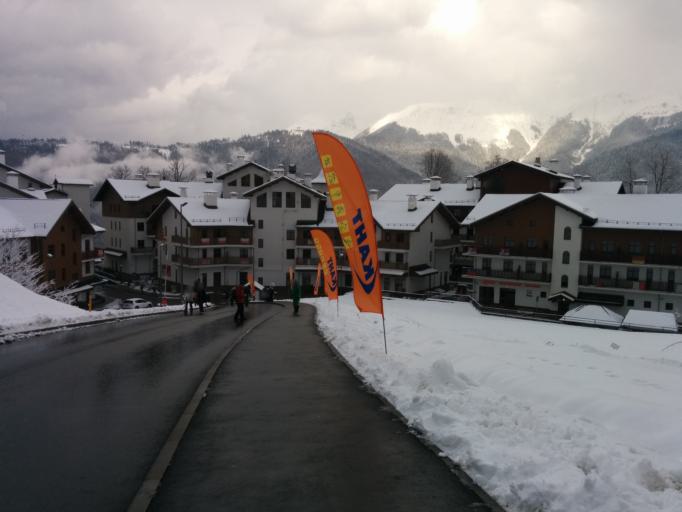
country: RU
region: Krasnodarskiy
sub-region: Sochi City
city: Krasnaya Polyana
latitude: 43.6589
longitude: 40.3203
